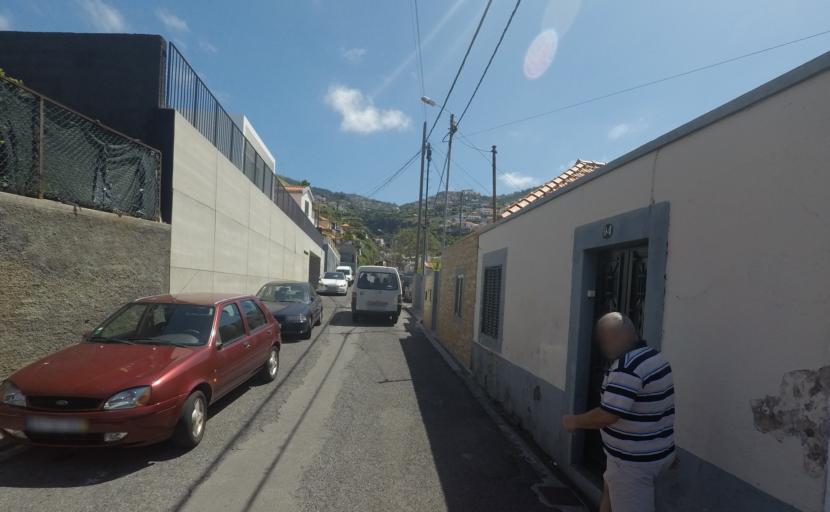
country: PT
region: Madeira
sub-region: Funchal
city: Funchal
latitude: 32.6474
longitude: -16.8890
